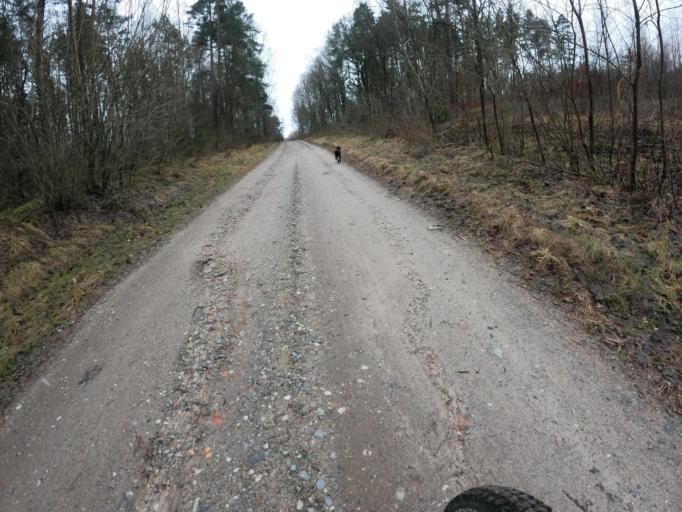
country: PL
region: West Pomeranian Voivodeship
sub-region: Powiat slawienski
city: Slawno
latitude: 54.2423
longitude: 16.6450
